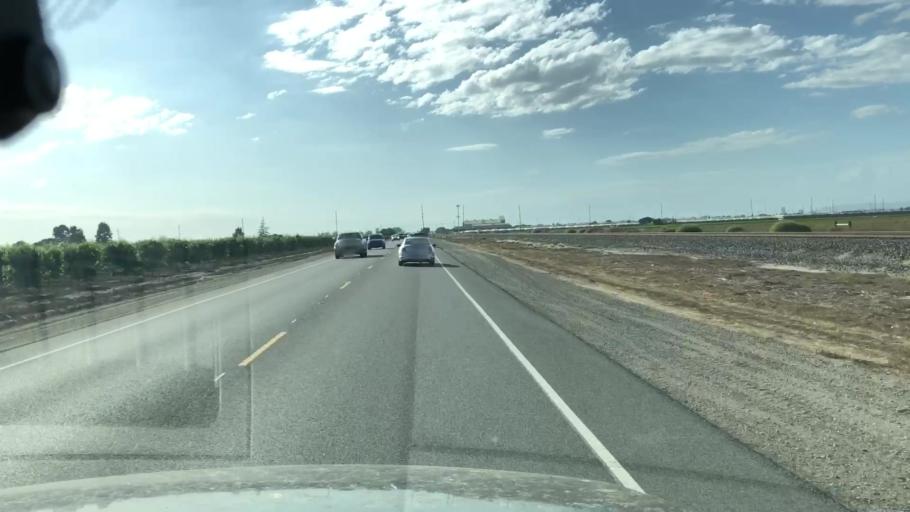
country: US
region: California
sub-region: Ventura County
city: Camarillo
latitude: 34.1965
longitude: -119.0883
